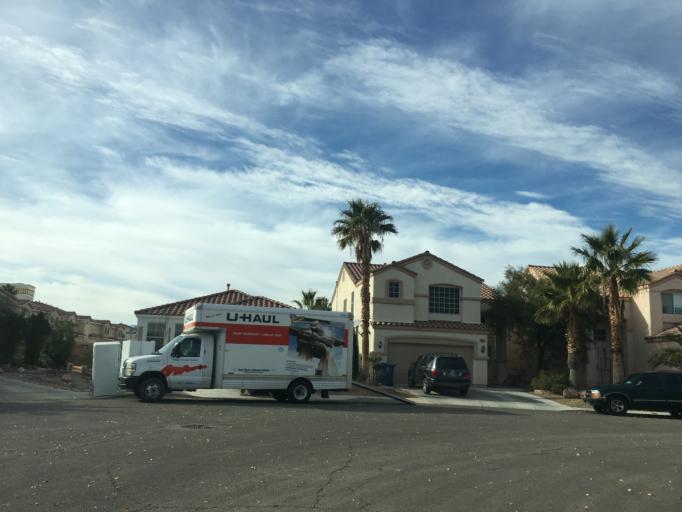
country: US
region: Nevada
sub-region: Clark County
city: Enterprise
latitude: 36.0143
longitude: -115.1682
